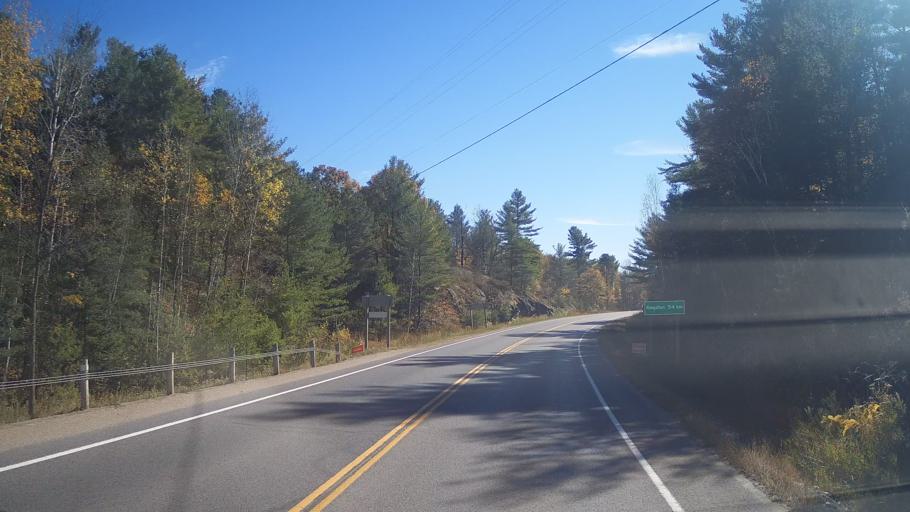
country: CA
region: Ontario
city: Skatepark
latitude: 44.6526
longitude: -76.7156
